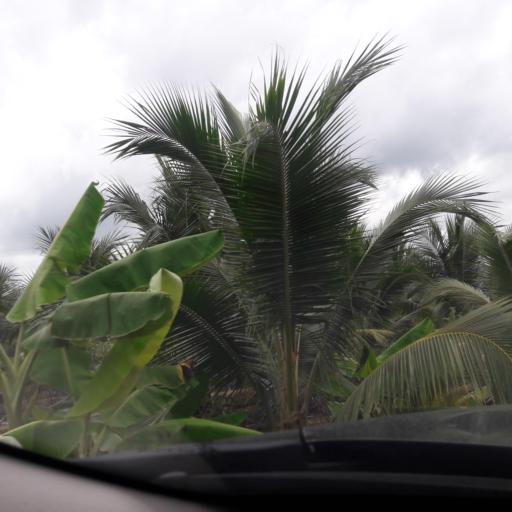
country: TH
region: Ratchaburi
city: Damnoen Saduak
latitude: 13.5775
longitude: 99.9486
